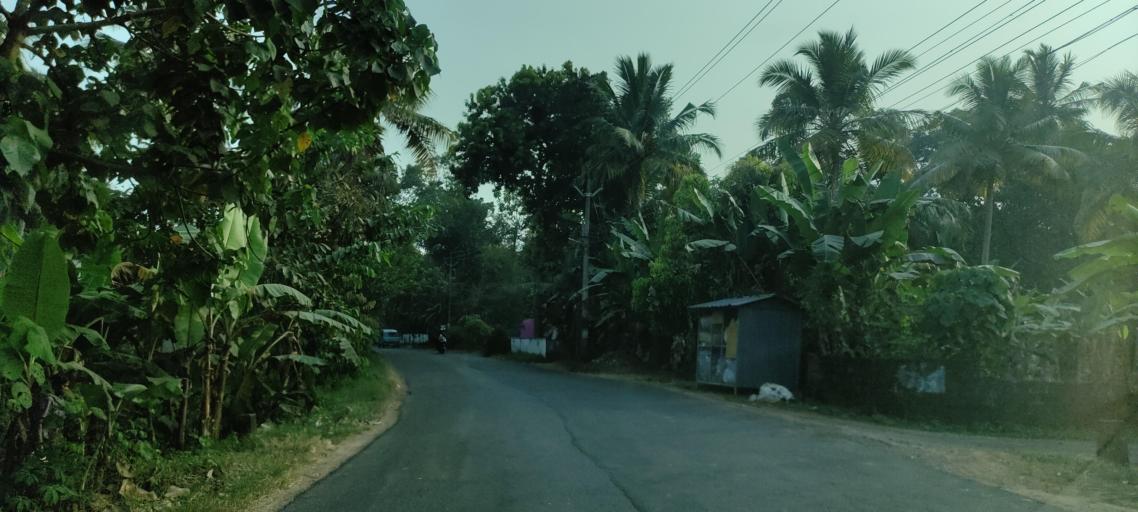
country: IN
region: Kerala
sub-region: Kottayam
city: Vaikam
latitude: 9.6895
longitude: 76.4636
